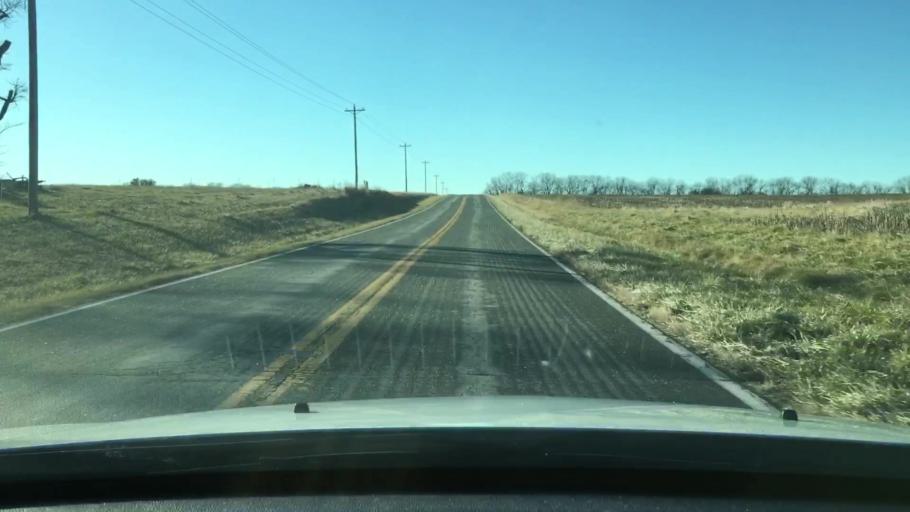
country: US
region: Missouri
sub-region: Audrain County
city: Mexico
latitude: 39.2766
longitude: -91.7854
